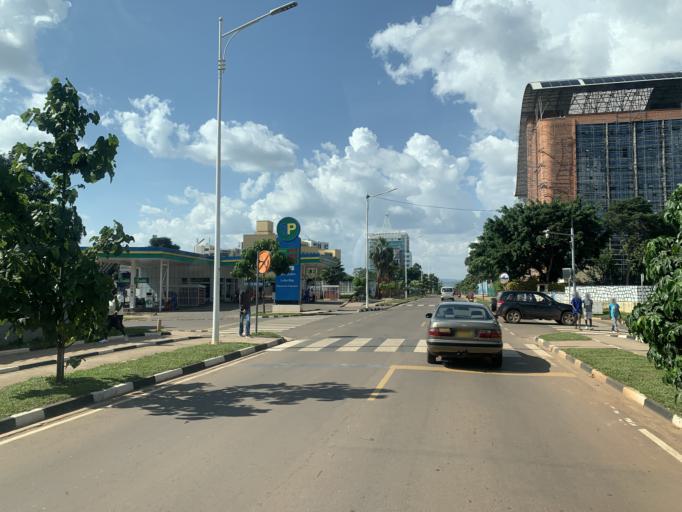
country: RW
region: Kigali
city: Kigali
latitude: -1.9506
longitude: 30.0614
